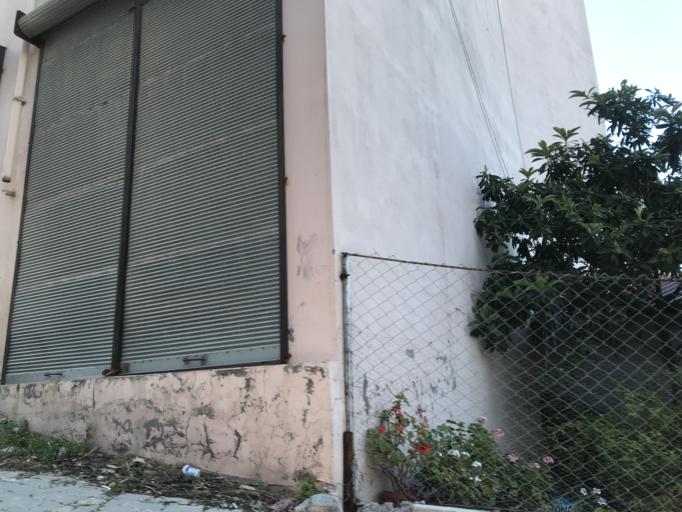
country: TR
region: Hatay
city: Samandag
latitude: 36.0817
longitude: 35.9812
